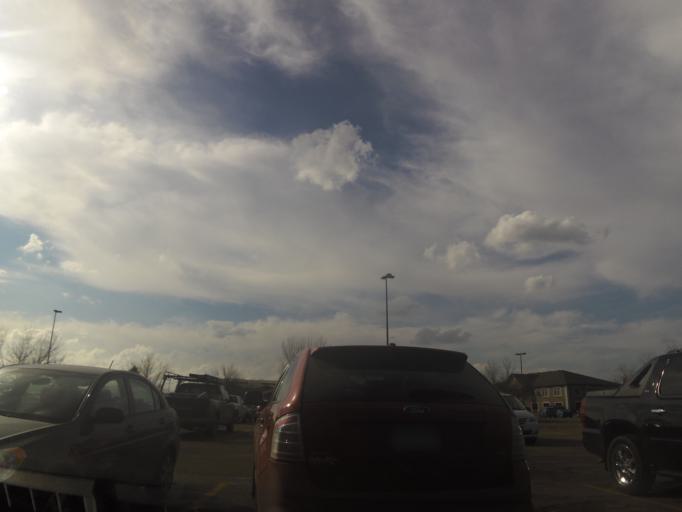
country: US
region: North Dakota
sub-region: Grand Forks County
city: Grand Forks
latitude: 47.8881
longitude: -97.0698
